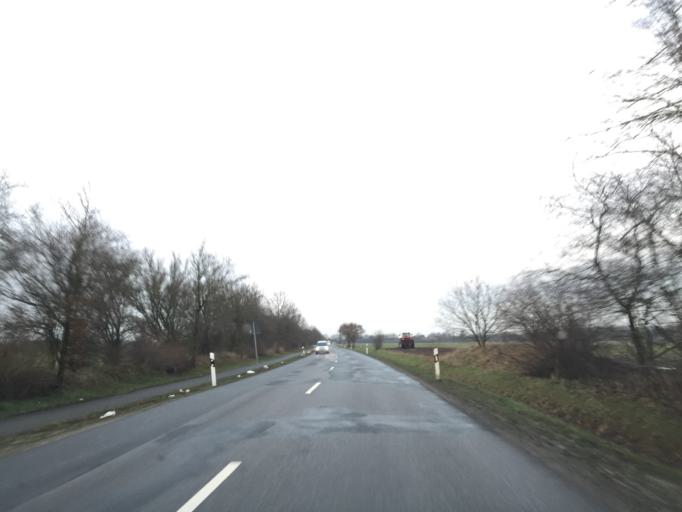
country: DE
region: Schleswig-Holstein
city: Wahlstedt
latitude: 53.9792
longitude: 10.1881
